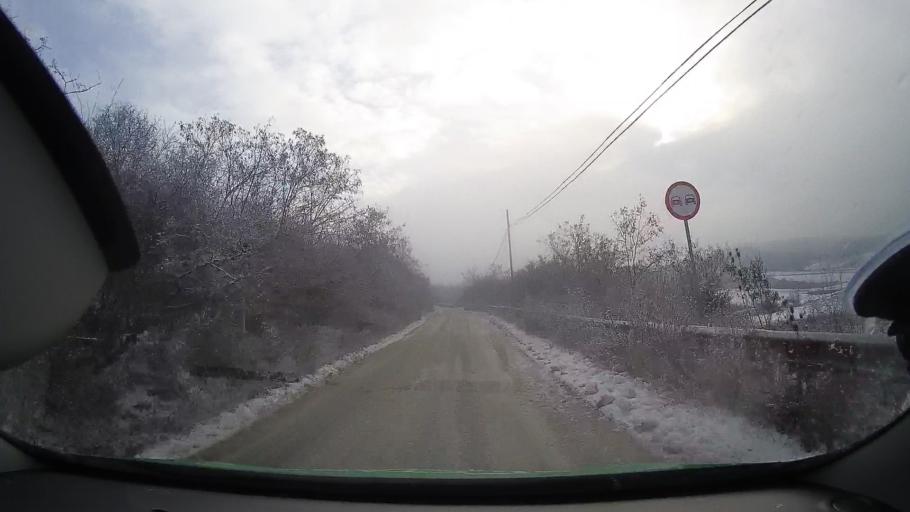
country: RO
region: Mures
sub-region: Comuna Chetani
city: Chetani
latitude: 46.4271
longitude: 24.0101
